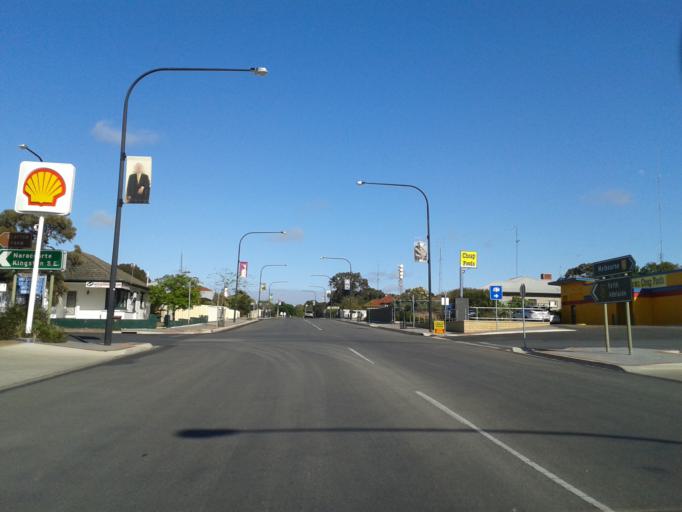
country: AU
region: South Australia
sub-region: Tatiara
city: Bordertown
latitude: -36.3082
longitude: 140.7725
